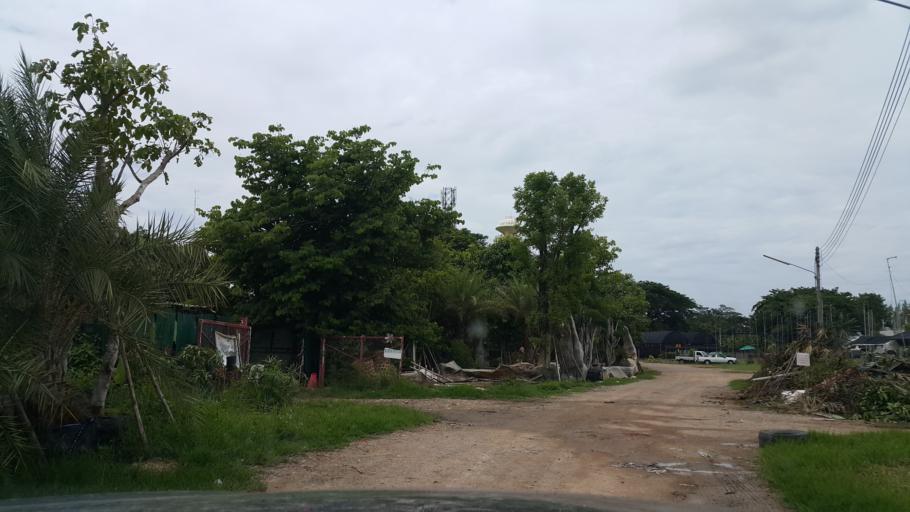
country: TH
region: Chiang Mai
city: Chiang Mai
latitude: 18.8073
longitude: 98.9979
